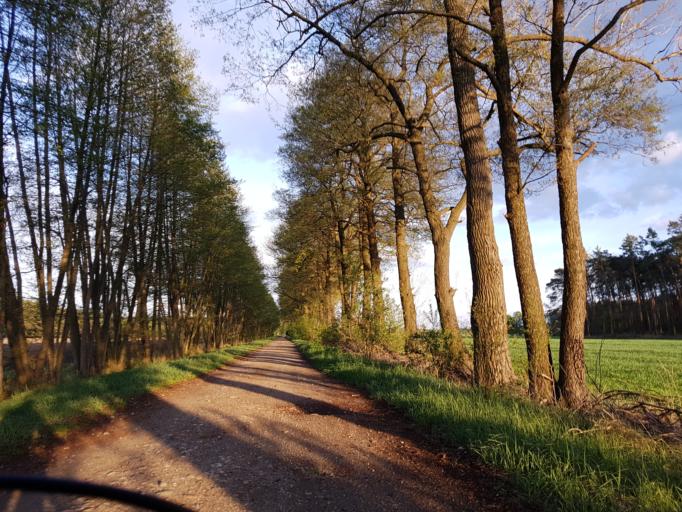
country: DE
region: Brandenburg
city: Schilda
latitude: 51.5736
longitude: 13.3732
